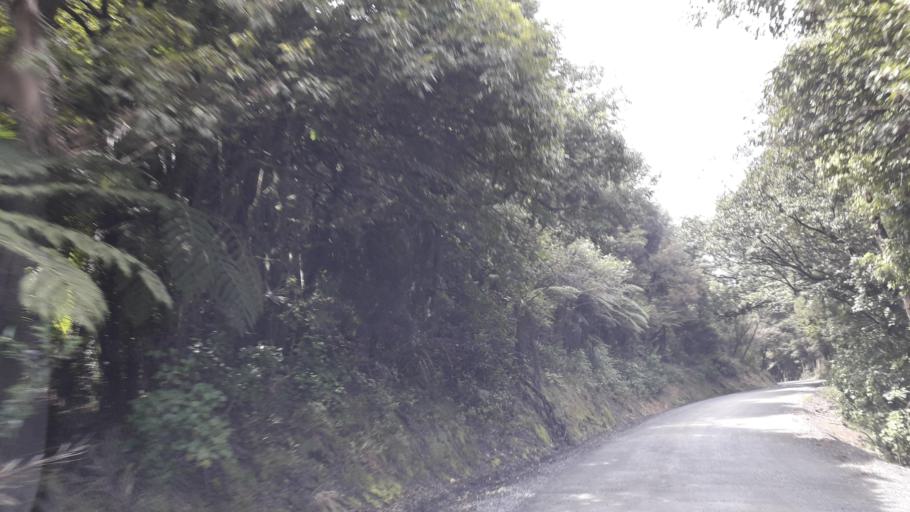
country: NZ
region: Northland
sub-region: Far North District
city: Kaitaia
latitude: -35.1698
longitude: 173.3391
